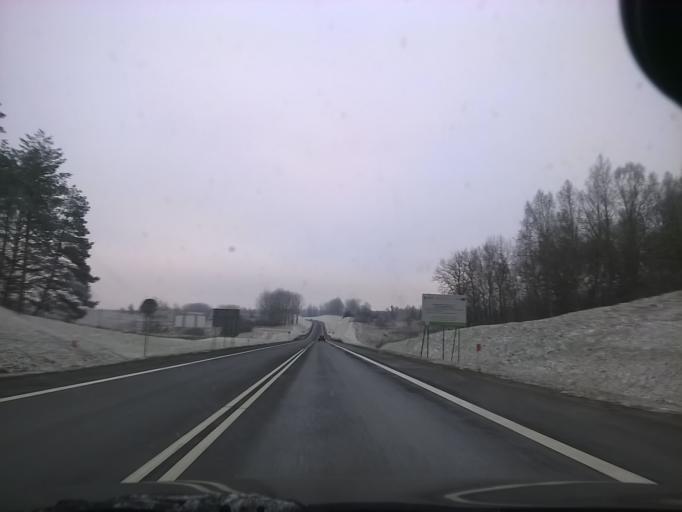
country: PL
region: Warmian-Masurian Voivodeship
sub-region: Powiat olsztynski
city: Czerwonka
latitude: 53.8282
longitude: 20.8434
